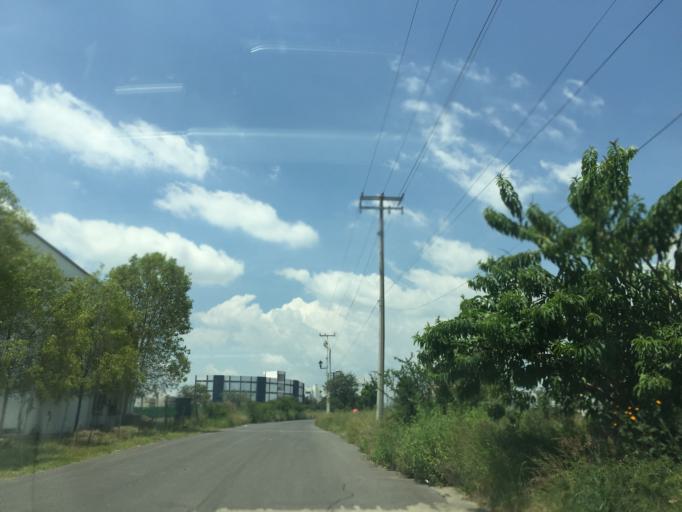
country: MX
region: Guanajuato
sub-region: Leon
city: La Ermita
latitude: 21.1530
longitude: -101.7175
